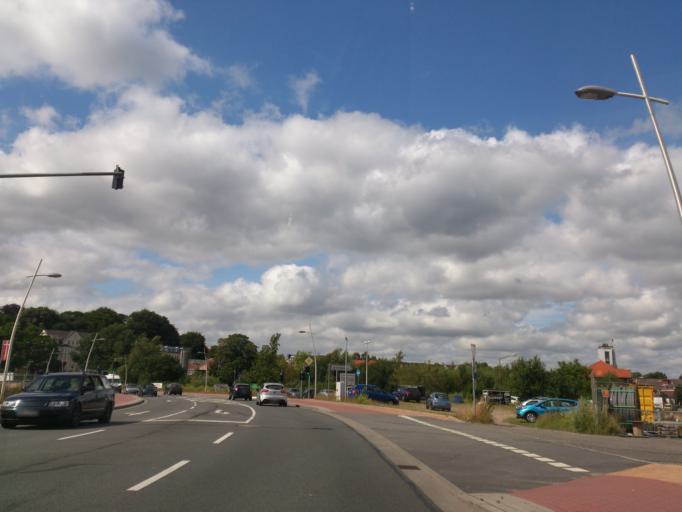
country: DE
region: Schleswig-Holstein
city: Flensburg
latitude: 54.7996
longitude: 9.4268
